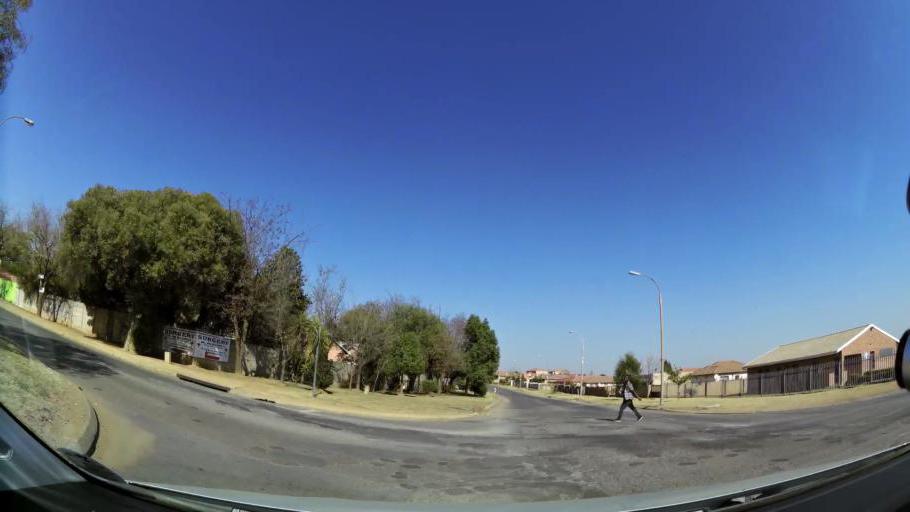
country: ZA
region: Gauteng
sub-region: Ekurhuleni Metropolitan Municipality
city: Tembisa
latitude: -26.0449
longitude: 28.2039
